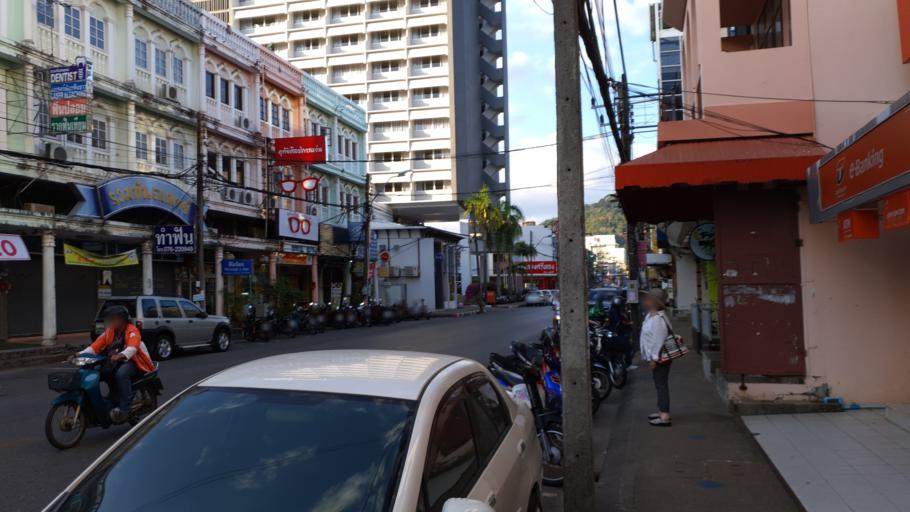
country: TH
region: Phuket
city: Ban Talat Nua
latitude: 7.8814
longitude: 98.3924
